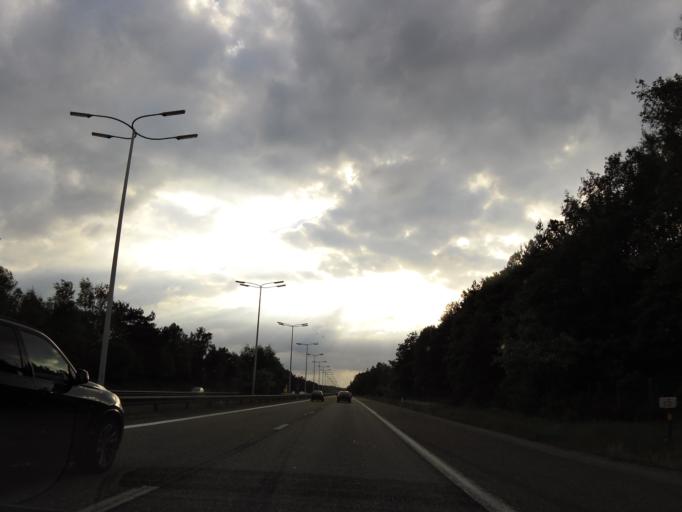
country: BE
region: Flanders
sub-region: Provincie Limburg
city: Maasmechelen
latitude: 50.9608
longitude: 5.6380
